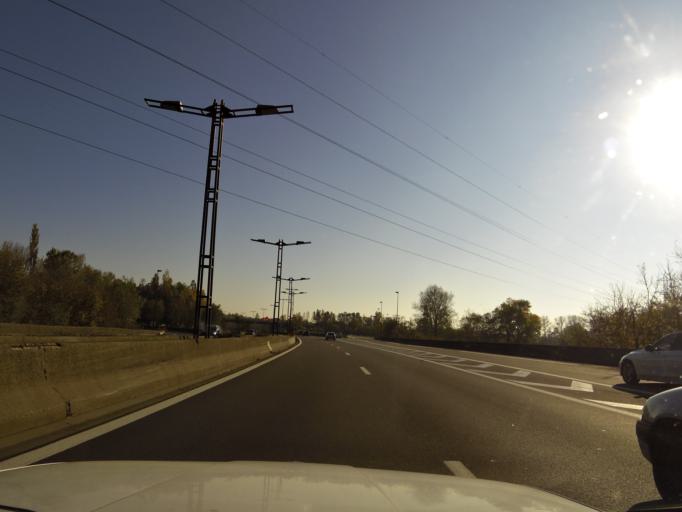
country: FR
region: Rhone-Alpes
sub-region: Departement du Rhone
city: Decines-Charpieu
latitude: 45.7862
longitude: 4.9561
